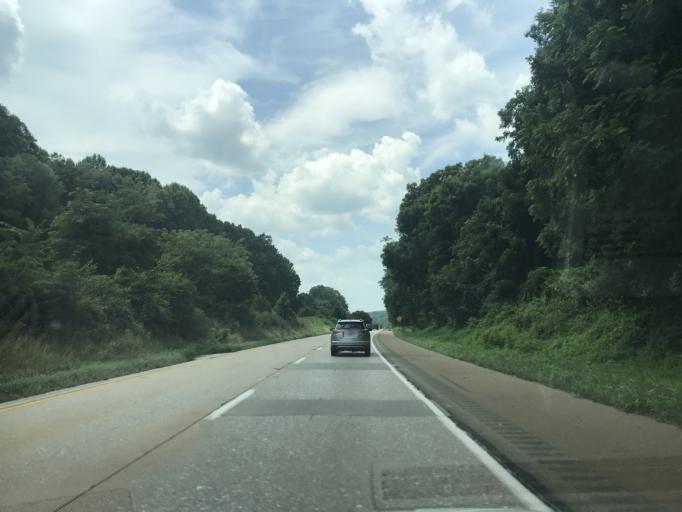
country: US
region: Pennsylvania
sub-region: Chester County
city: Toughkenamon
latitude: 39.8462
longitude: -75.7706
